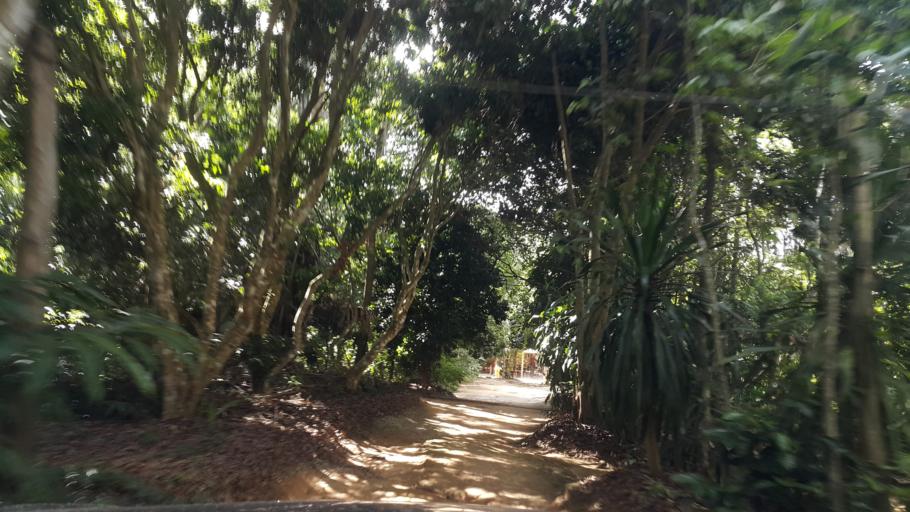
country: TH
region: Loei
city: Na Haeo
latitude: 17.5560
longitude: 100.9548
